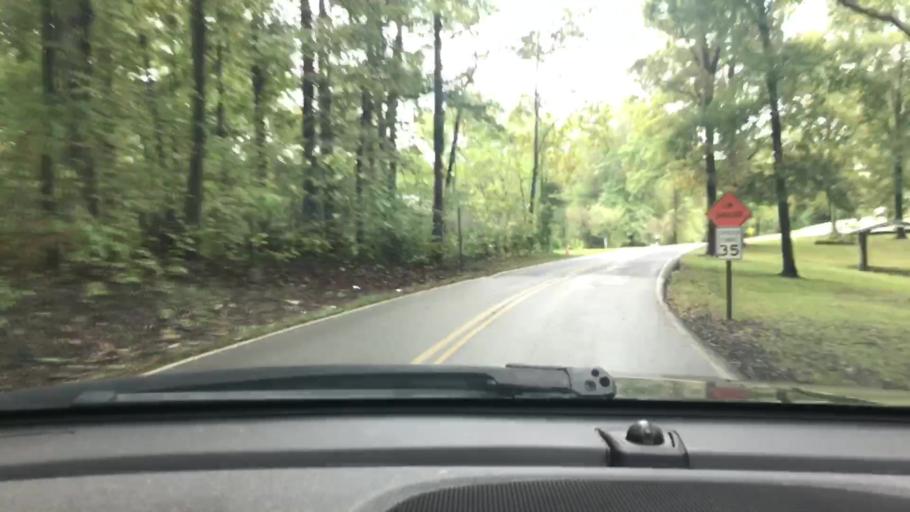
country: US
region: Tennessee
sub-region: Cheatham County
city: Kingston Springs
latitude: 36.1017
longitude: -87.1364
